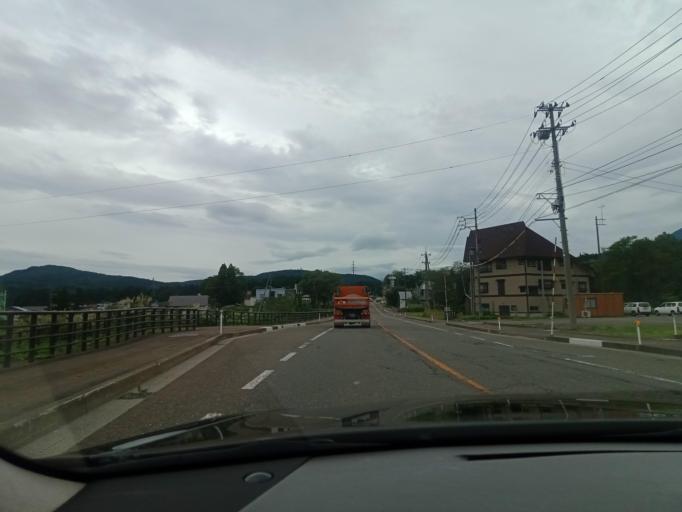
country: JP
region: Niigata
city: Arai
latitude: 36.8825
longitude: 138.2054
